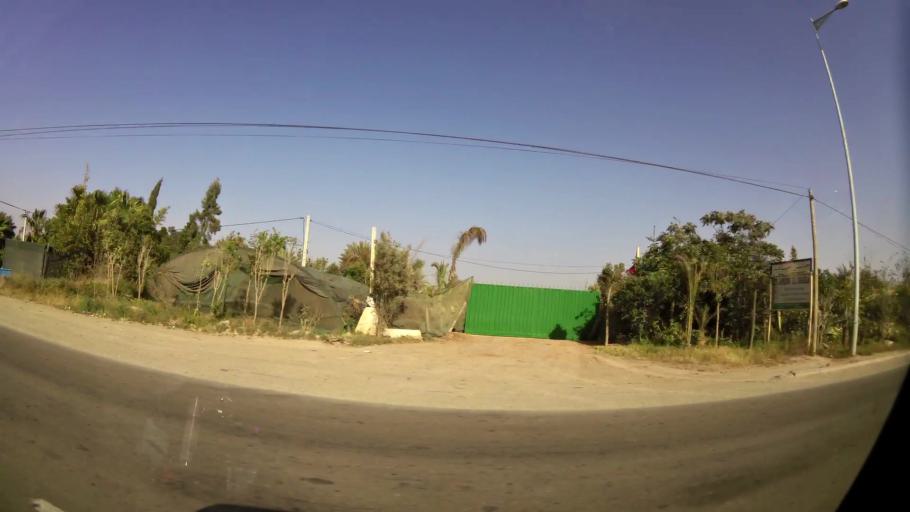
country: MA
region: Souss-Massa-Draa
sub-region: Inezgane-Ait Mellou
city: Inezgane
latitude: 30.3641
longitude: -9.5060
